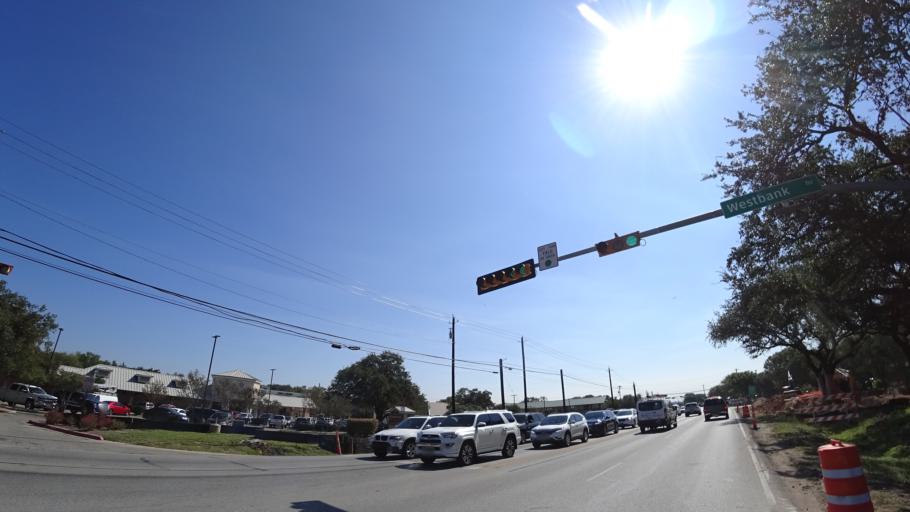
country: US
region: Texas
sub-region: Travis County
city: Rollingwood
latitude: 30.2798
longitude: -97.8073
